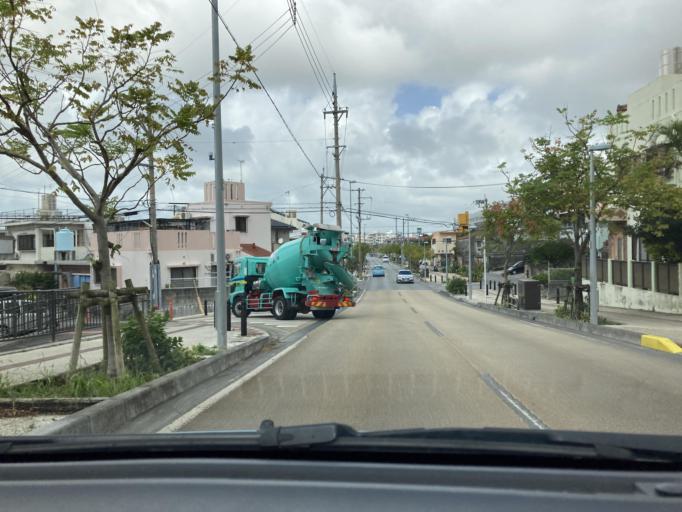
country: JP
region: Okinawa
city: Ginowan
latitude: 26.2291
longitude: 127.7323
